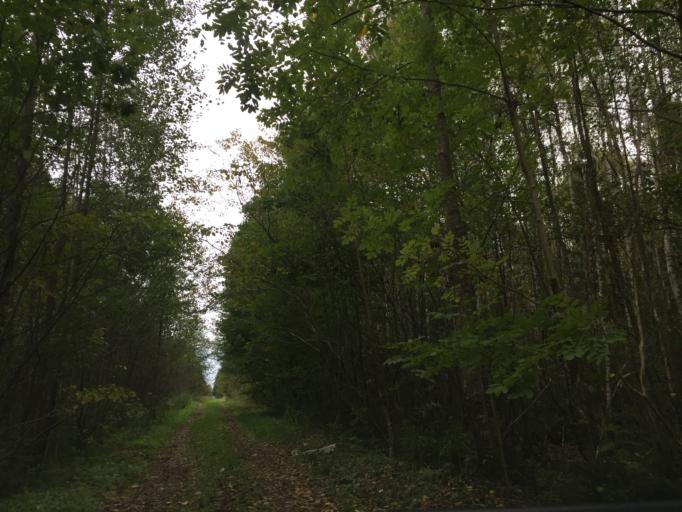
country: LV
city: Tireli
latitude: 56.8928
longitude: 23.5535
